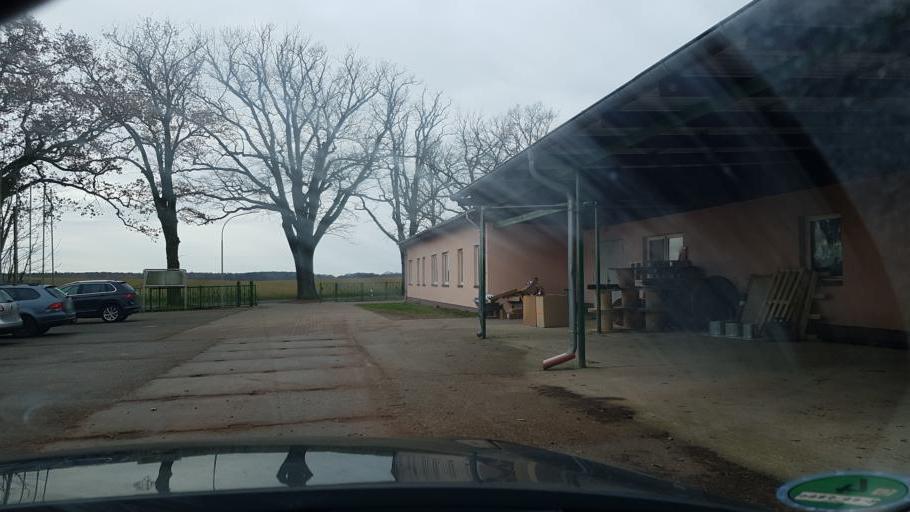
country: DE
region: Brandenburg
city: Kyritz
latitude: 52.9461
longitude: 12.3760
